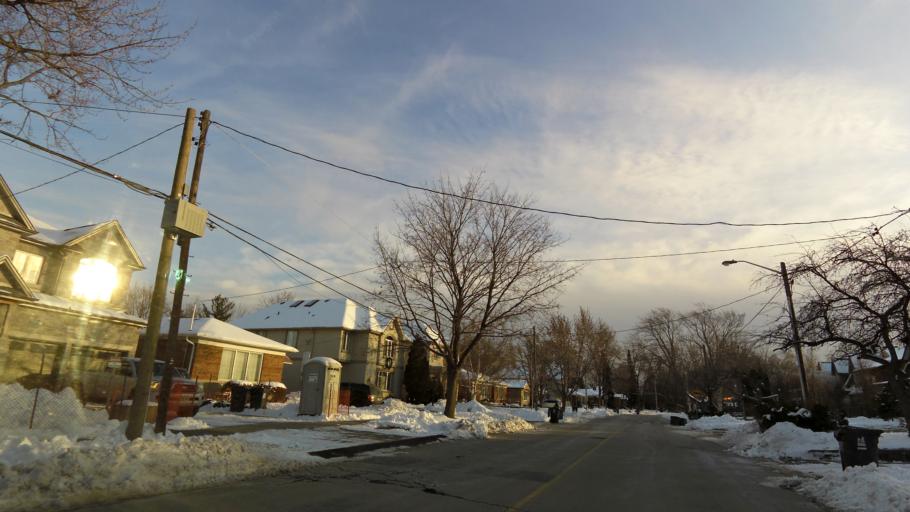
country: CA
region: Ontario
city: Etobicoke
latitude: 43.6476
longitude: -79.5515
